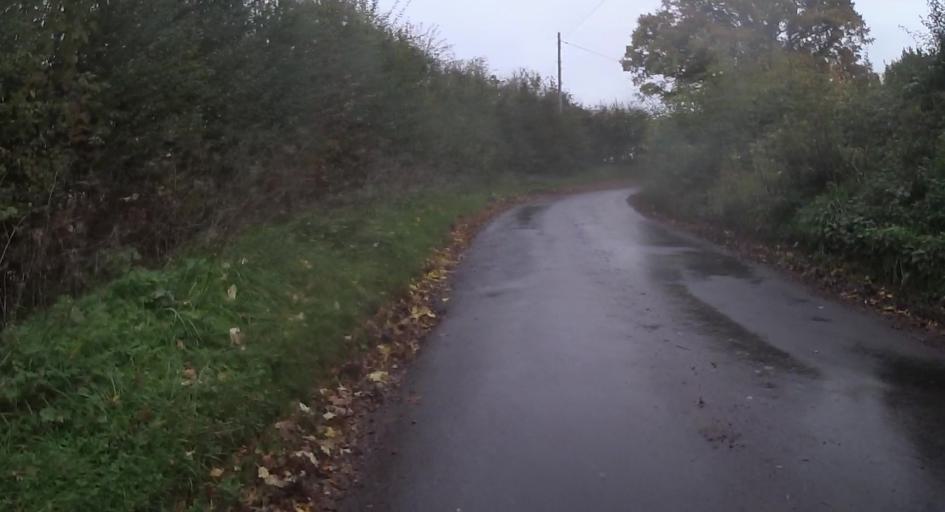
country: GB
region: England
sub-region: Surrey
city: Farnham
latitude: 51.2025
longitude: -0.8510
